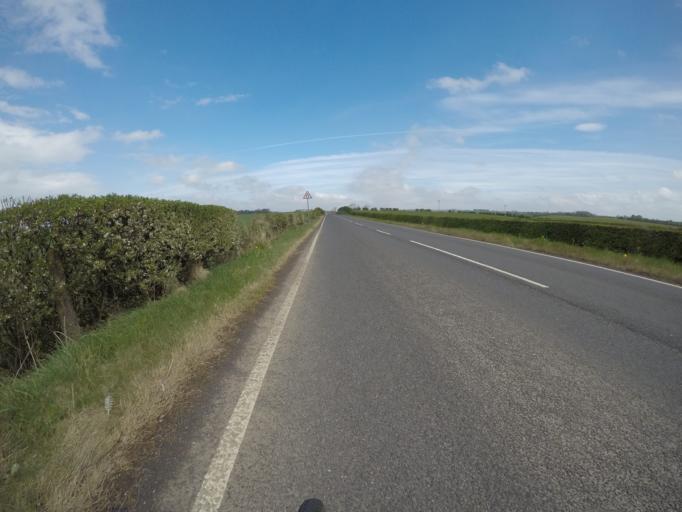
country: GB
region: Scotland
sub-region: East Ayrshire
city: Kilmaurs
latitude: 55.6568
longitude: -4.5564
